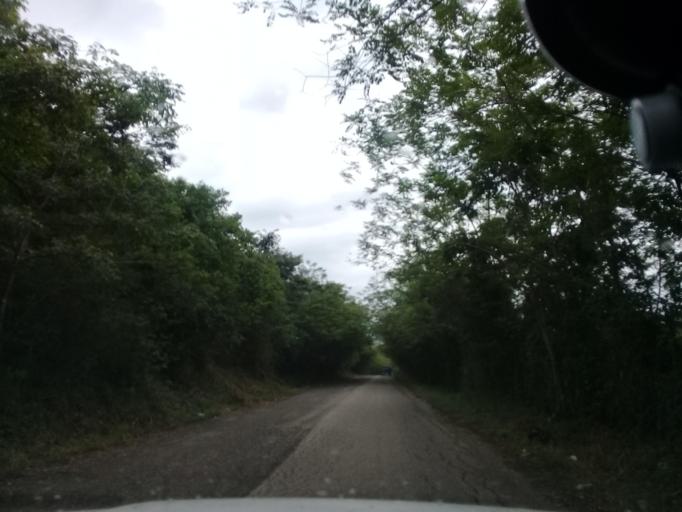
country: MX
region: Veracruz
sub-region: Chalma
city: San Pedro Coyutla
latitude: 21.2095
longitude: -98.3856
